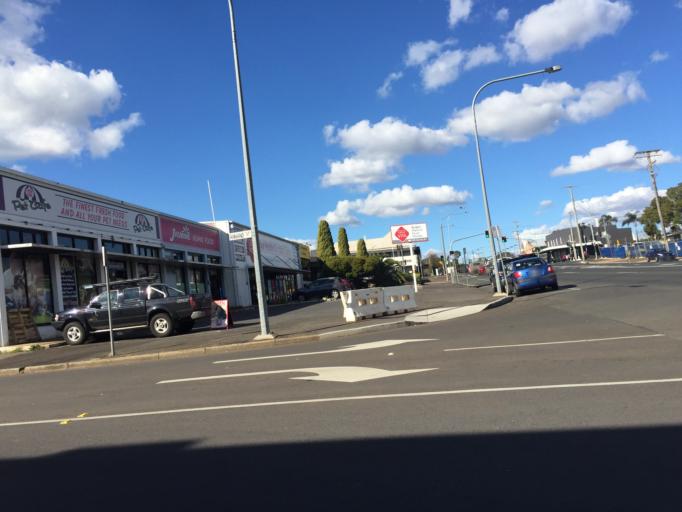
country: AU
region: Queensland
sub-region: Toowoomba
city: Toowoomba
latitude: -27.5649
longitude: 151.9537
